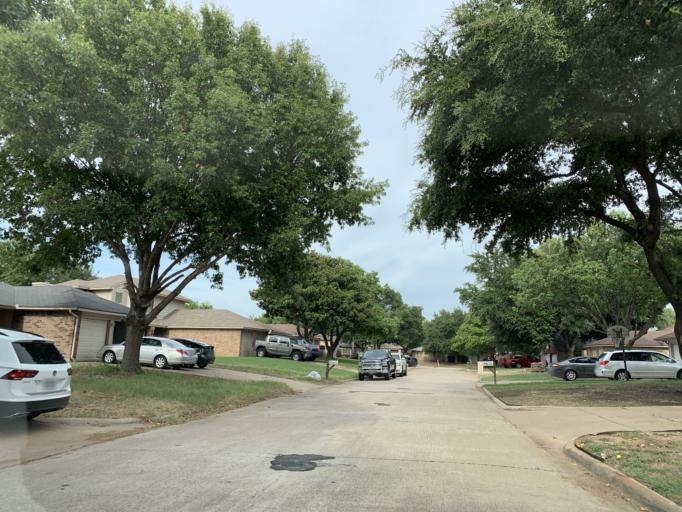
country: US
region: Texas
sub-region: Dallas County
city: Grand Prairie
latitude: 32.6671
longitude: -97.0452
